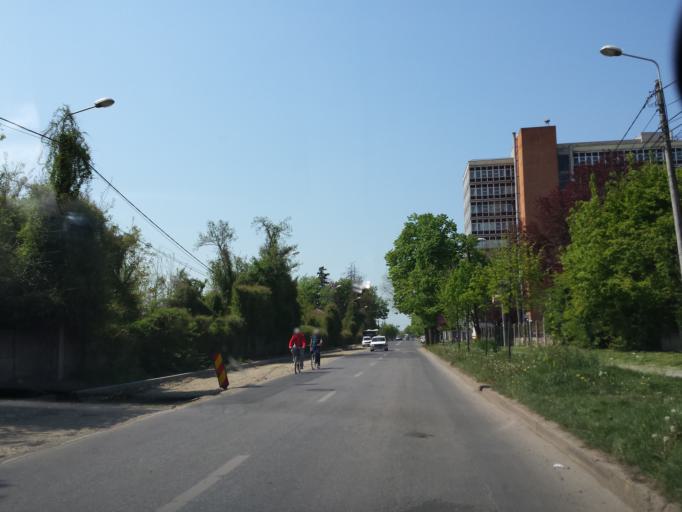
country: RO
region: Timis
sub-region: Comuna Dumbravita
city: Dumbravita
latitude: 45.7751
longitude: 21.2620
